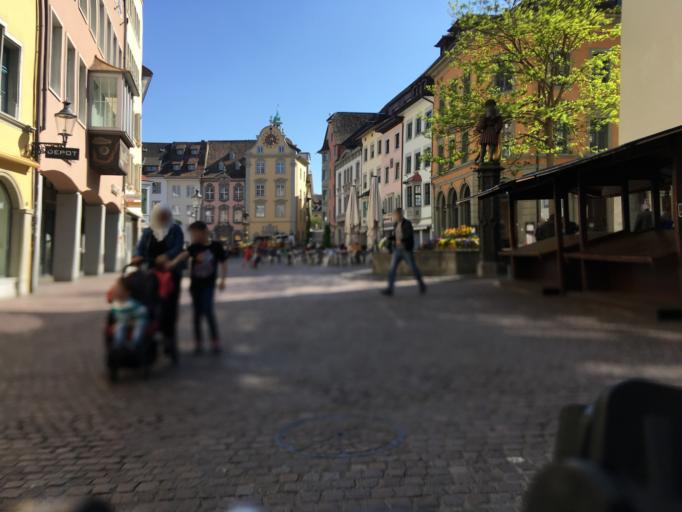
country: CH
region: Schaffhausen
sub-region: Bezirk Schaffhausen
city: Schaffhausen
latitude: 47.6973
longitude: 8.6334
